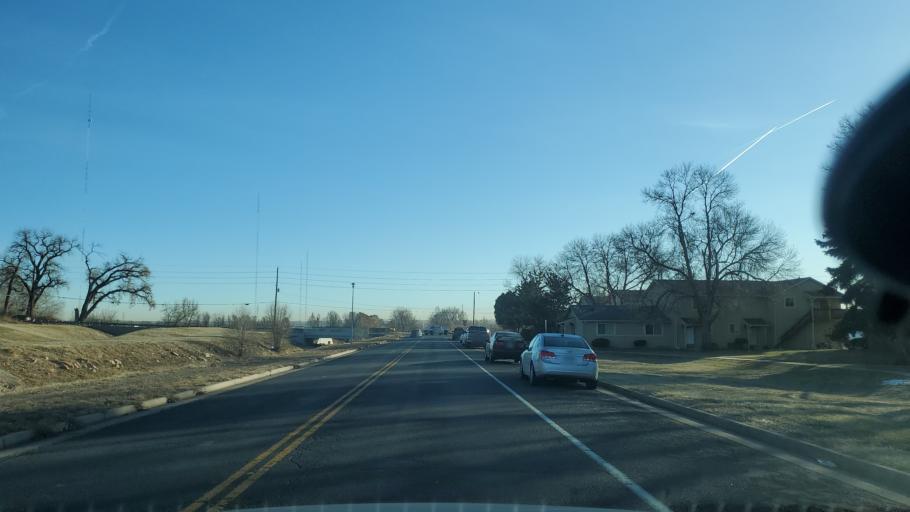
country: US
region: Colorado
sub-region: Adams County
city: Welby
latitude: 39.8418
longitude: -104.9608
